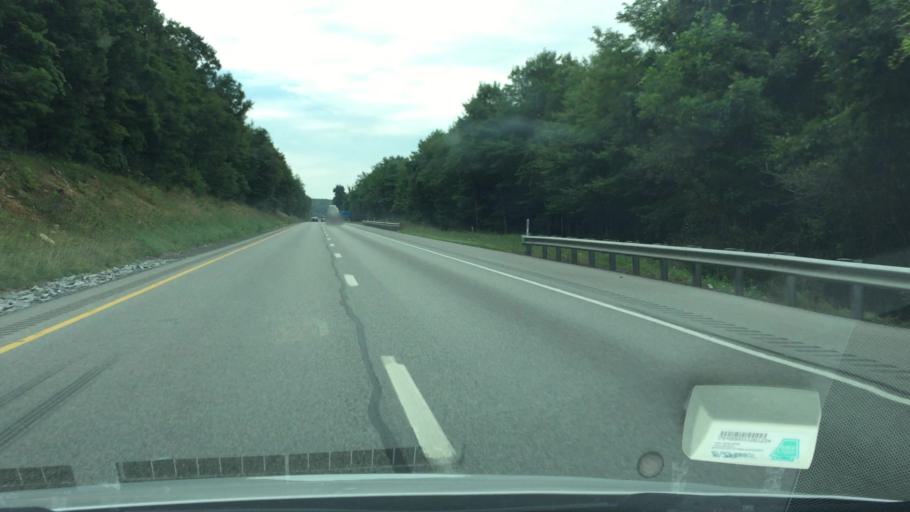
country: US
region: Pennsylvania
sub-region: Bedford County
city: Earlston
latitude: 39.8977
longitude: -78.2410
